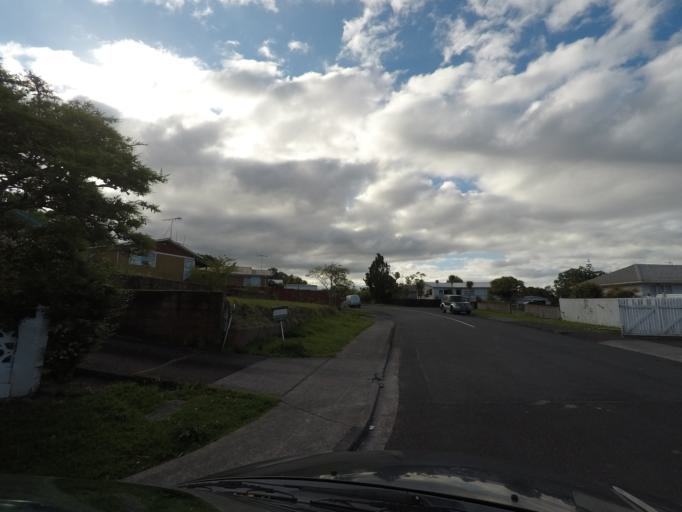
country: NZ
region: Auckland
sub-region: Auckland
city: Rosebank
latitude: -36.8833
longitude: 174.6534
